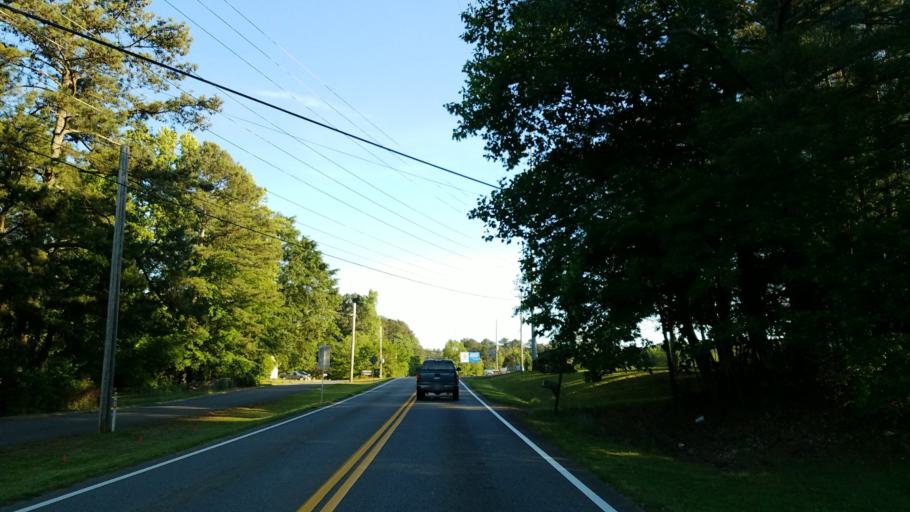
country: US
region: Georgia
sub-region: Cherokee County
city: Woodstock
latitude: 34.1272
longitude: -84.5860
